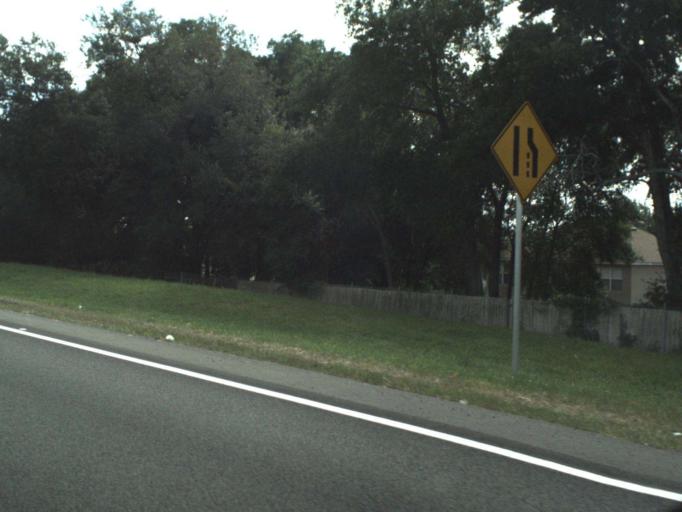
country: US
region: Florida
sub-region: Seminole County
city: Heathrow
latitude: 28.7290
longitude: -81.3728
